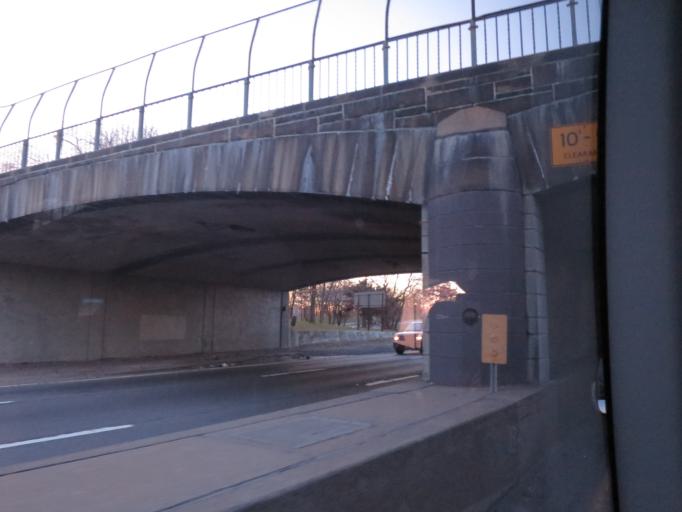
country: US
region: New York
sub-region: Queens County
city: Borough of Queens
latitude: 40.6664
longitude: -73.8348
